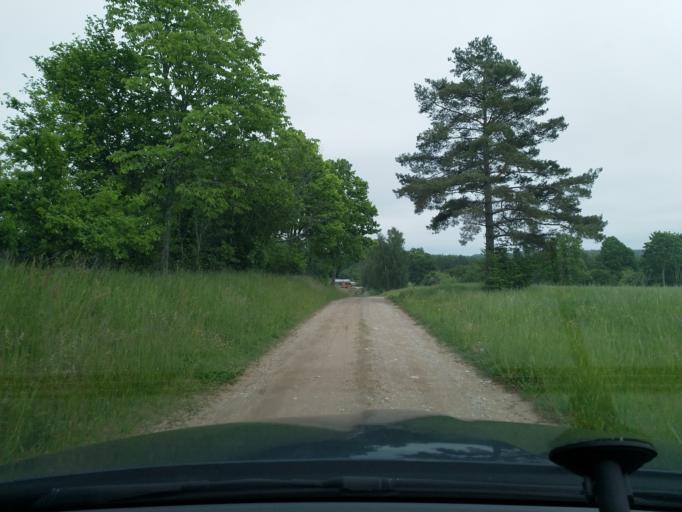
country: LV
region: Kuldigas Rajons
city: Kuldiga
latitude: 56.8779
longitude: 21.8254
